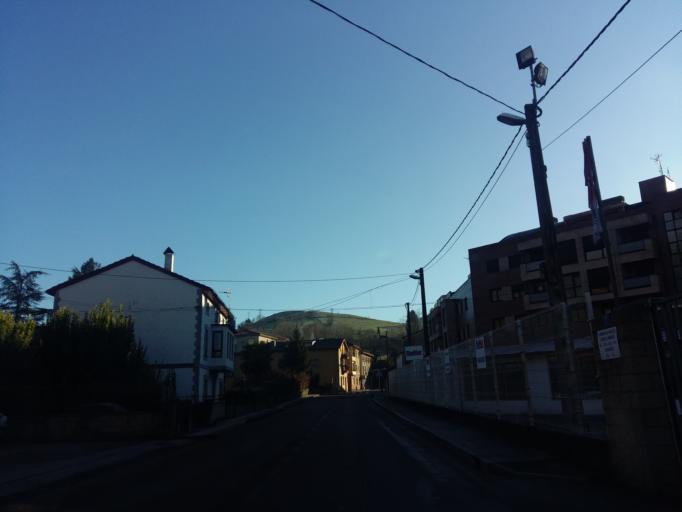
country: ES
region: Cantabria
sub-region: Provincia de Cantabria
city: Ramales de la Victoria
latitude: 43.2612
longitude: -3.4680
